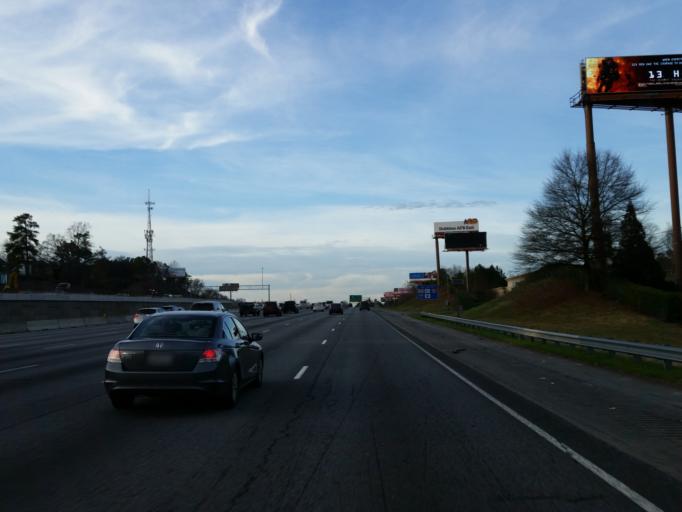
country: US
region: Georgia
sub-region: Cobb County
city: Smyrna
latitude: 33.9123
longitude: -84.4789
